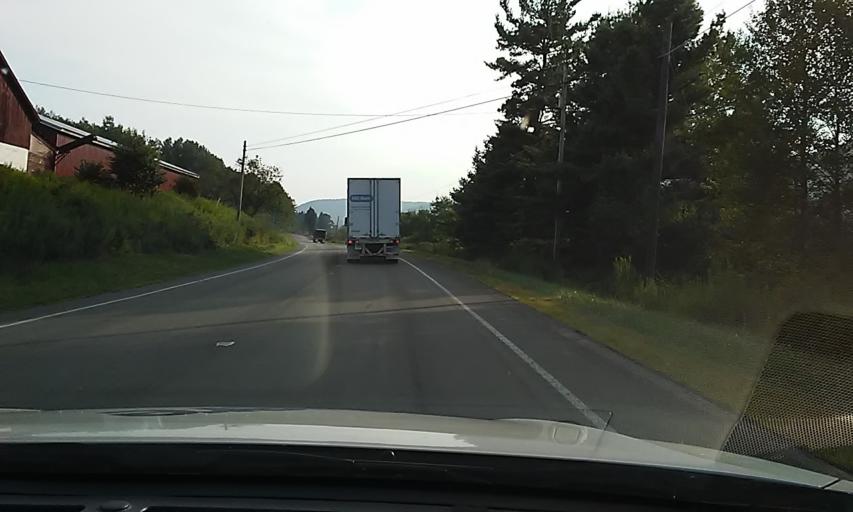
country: US
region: Pennsylvania
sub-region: McKean County
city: Smethport
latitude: 41.7782
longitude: -78.5053
